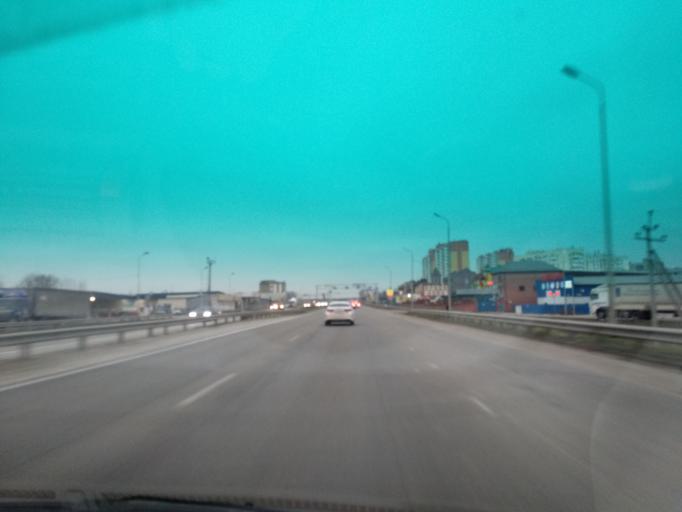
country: RU
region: Krasnodarskiy
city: Pashkovskiy
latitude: 45.0368
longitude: 39.1284
